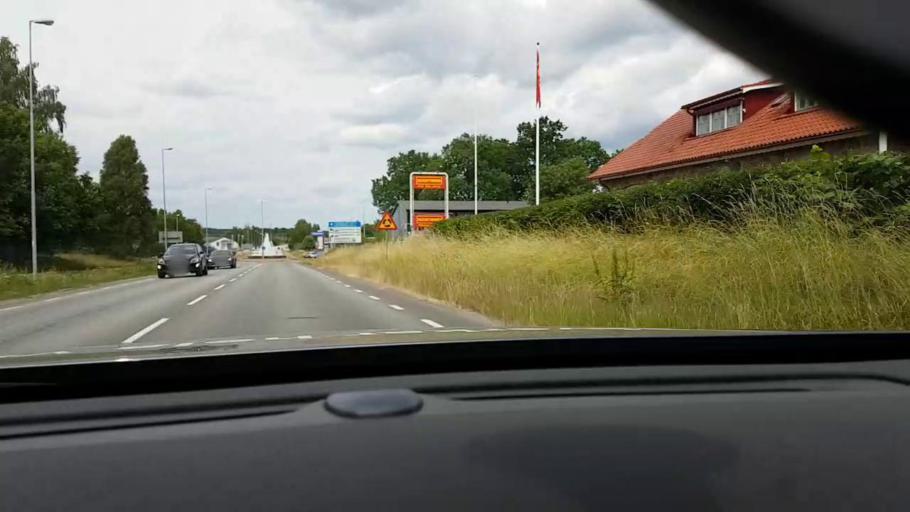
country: SE
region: Skane
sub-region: Hassleholms Kommun
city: Hassleholm
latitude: 56.1674
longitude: 13.7579
